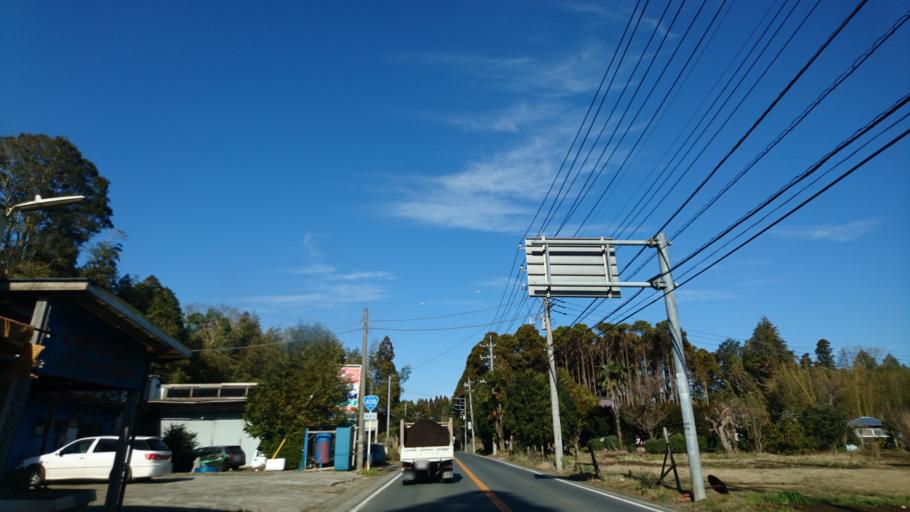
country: JP
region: Chiba
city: Yachimata
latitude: 35.6161
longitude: 140.3202
